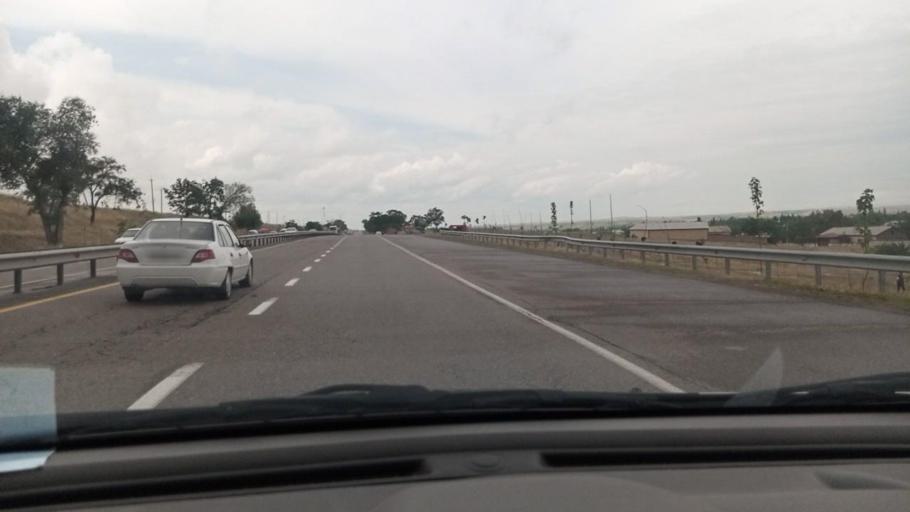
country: UZ
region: Toshkent
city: Ohangaron
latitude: 40.9746
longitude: 69.5448
